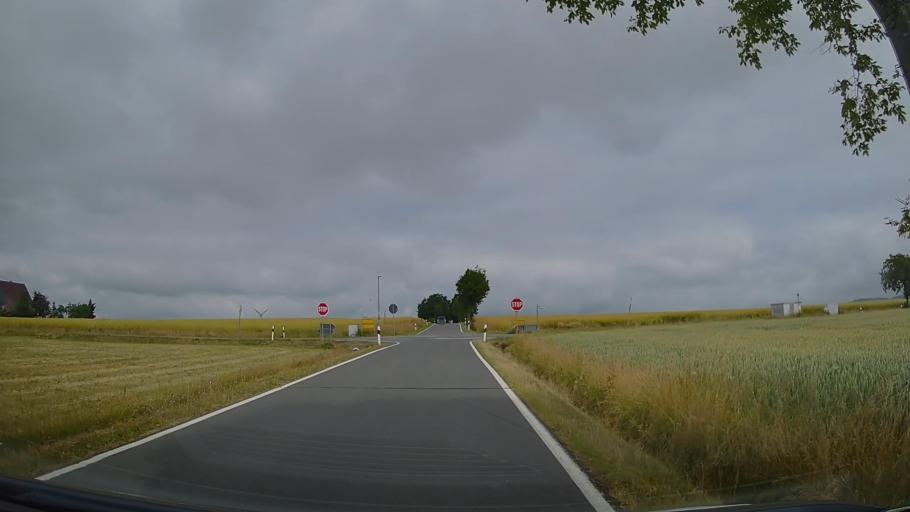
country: DE
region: Lower Saxony
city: Rinteln
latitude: 52.0963
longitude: 9.1266
